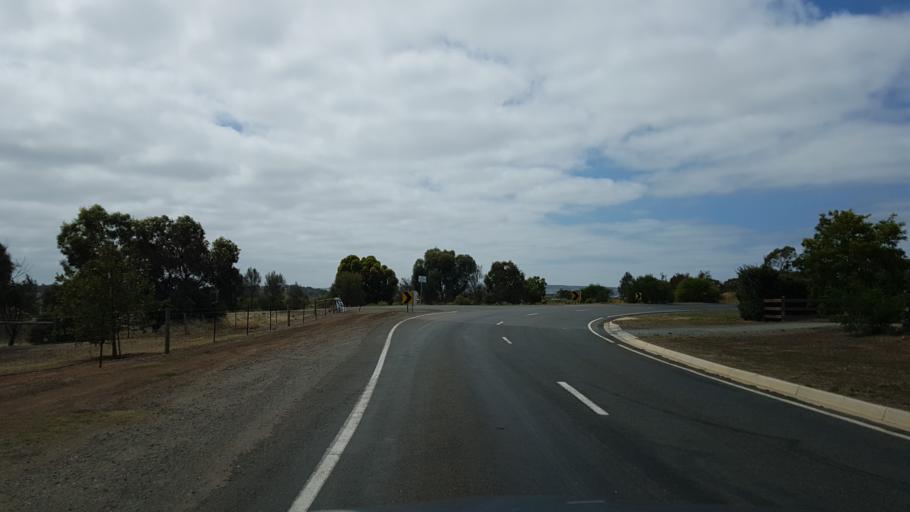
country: AU
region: South Australia
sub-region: Onkaparinga
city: McLaren Vale
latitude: -35.2102
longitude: 138.5221
